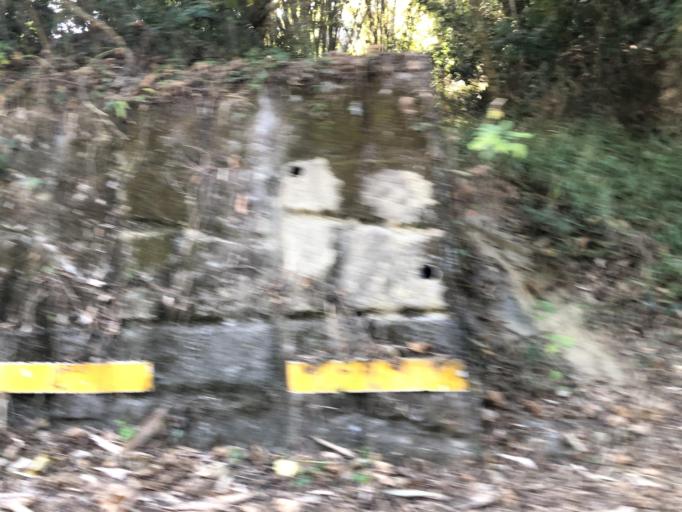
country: TW
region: Taiwan
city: Yujing
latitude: 23.0155
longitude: 120.3846
